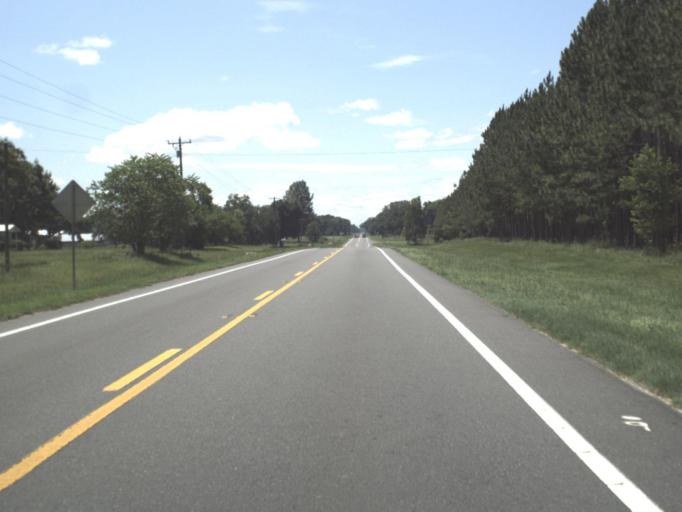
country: US
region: Florida
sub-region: Lafayette County
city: Mayo
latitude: 30.0947
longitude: -83.2336
